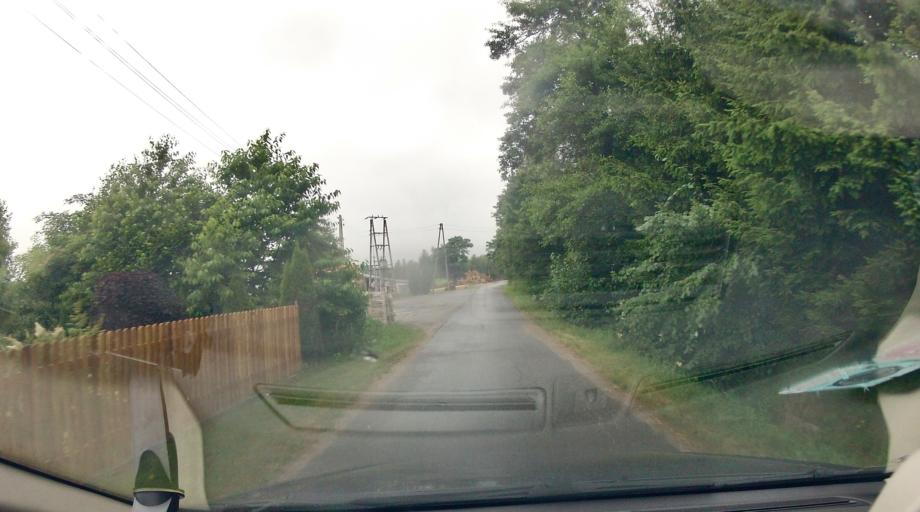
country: PL
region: Lower Silesian Voivodeship
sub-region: Powiat klodzki
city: Miedzylesie
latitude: 50.1839
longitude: 16.7261
